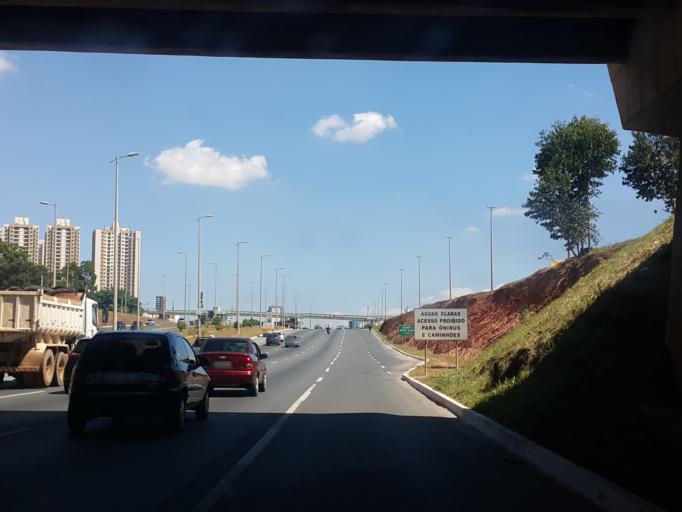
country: BR
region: Federal District
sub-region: Brasilia
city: Brasilia
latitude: -15.8301
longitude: -48.0391
